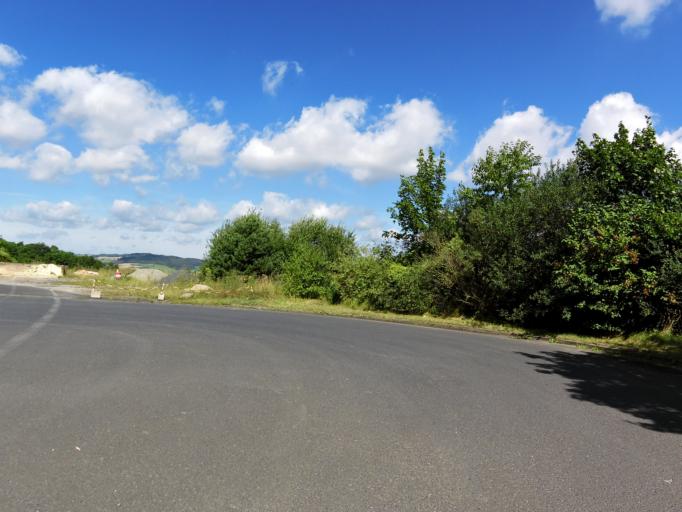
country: DE
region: Thuringia
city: Krauthausen
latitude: 51.0141
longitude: 10.2475
